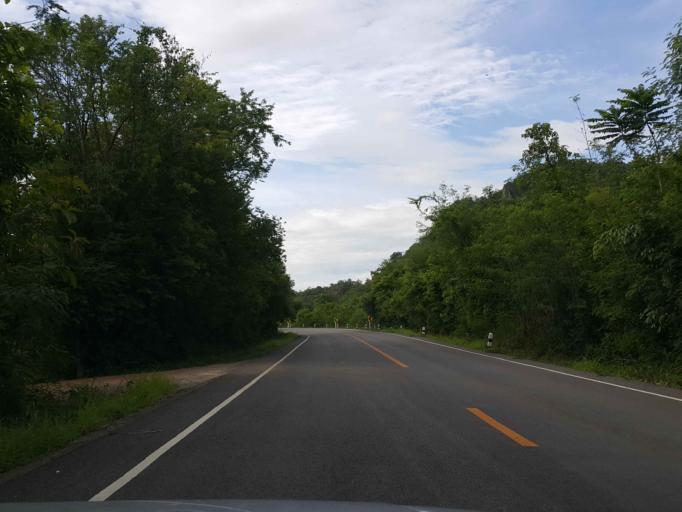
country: TH
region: Sukhothai
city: Thung Saliam
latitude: 17.2829
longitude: 99.5273
